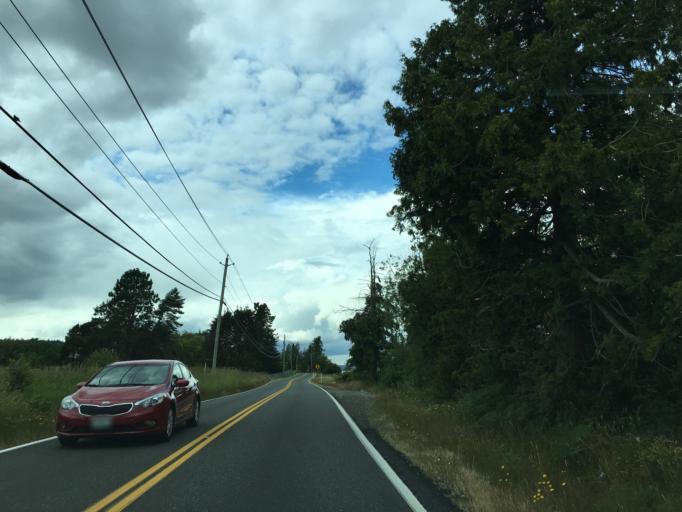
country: US
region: Washington
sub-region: Whatcom County
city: Blaine
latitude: 48.9579
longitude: -122.7504
